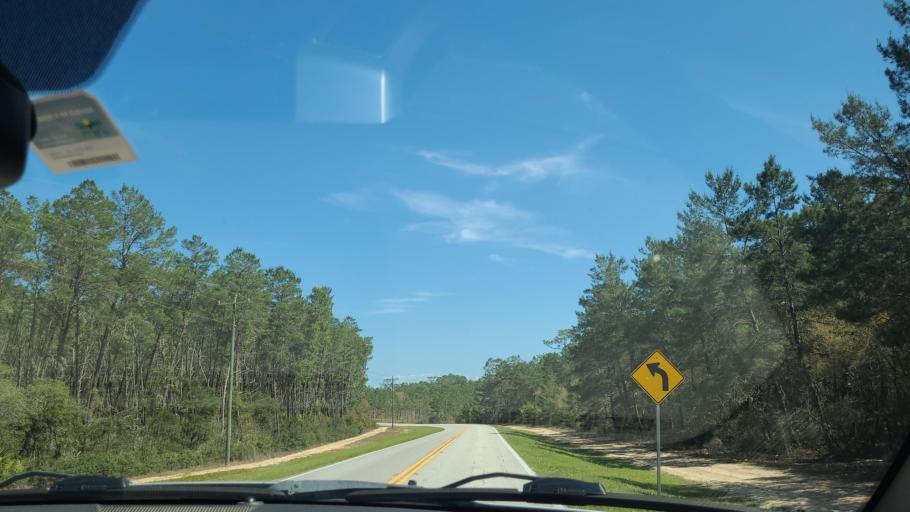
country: US
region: Florida
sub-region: Putnam County
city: Interlachen
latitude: 29.3674
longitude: -81.8323
